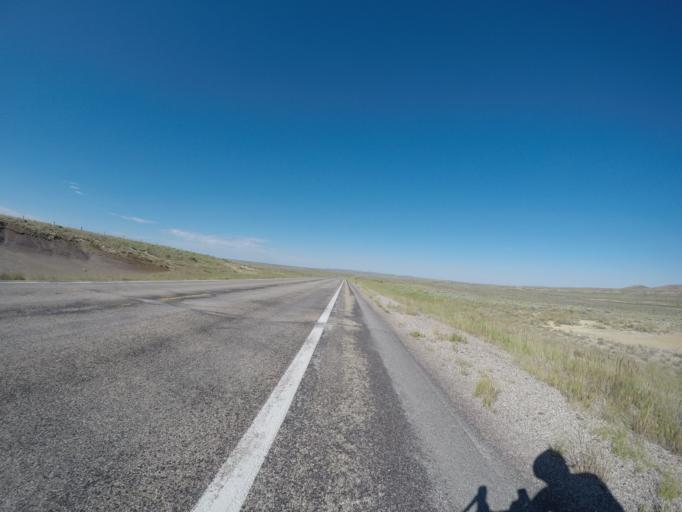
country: US
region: Wyoming
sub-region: Carbon County
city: Saratoga
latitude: 41.8784
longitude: -106.4882
